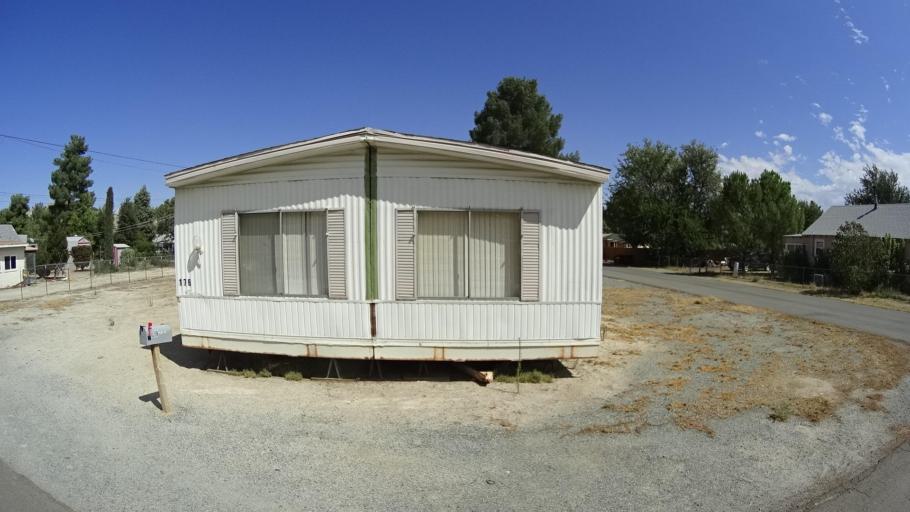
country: MX
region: Baja California
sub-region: Tecate
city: Cereso del Hongo
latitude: 32.6186
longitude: -116.1860
